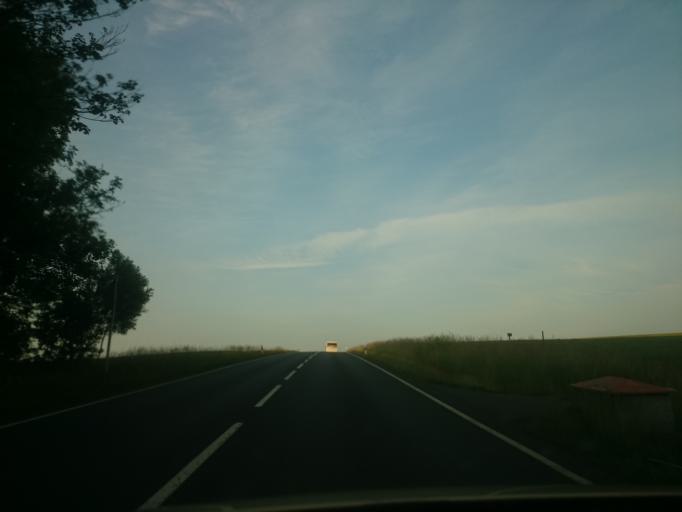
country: DE
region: Saxony
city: Grosshartmannsdorf
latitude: 50.8191
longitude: 13.3256
